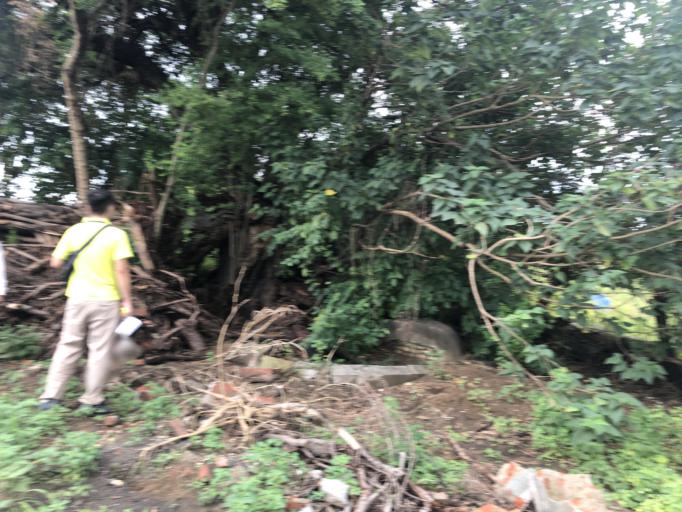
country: TW
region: Taiwan
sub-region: Tainan
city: Tainan
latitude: 22.9667
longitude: 120.1989
